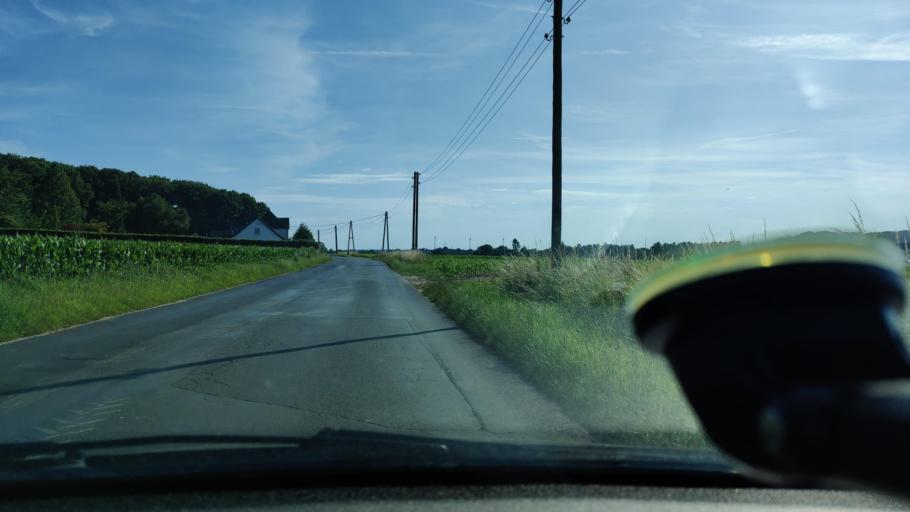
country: DE
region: North Rhine-Westphalia
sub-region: Regierungsbezirk Dusseldorf
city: Kamp-Lintfort
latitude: 51.5164
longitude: 6.5147
